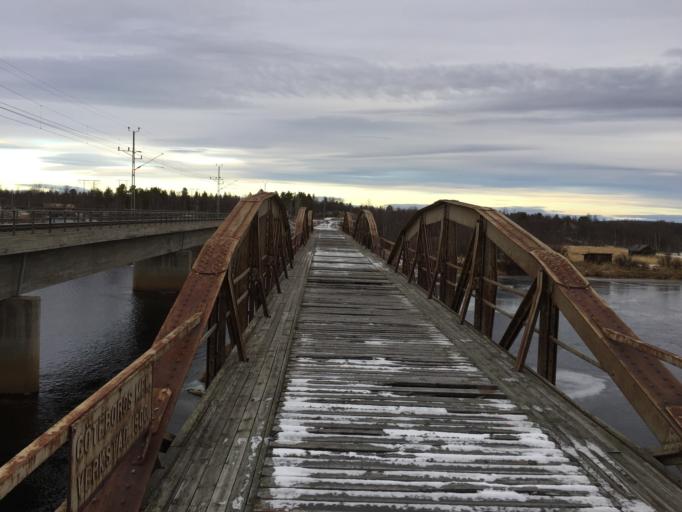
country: SE
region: Norrbotten
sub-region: Kiruna Kommun
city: Kiruna
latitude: 67.5405
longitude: 20.1004
